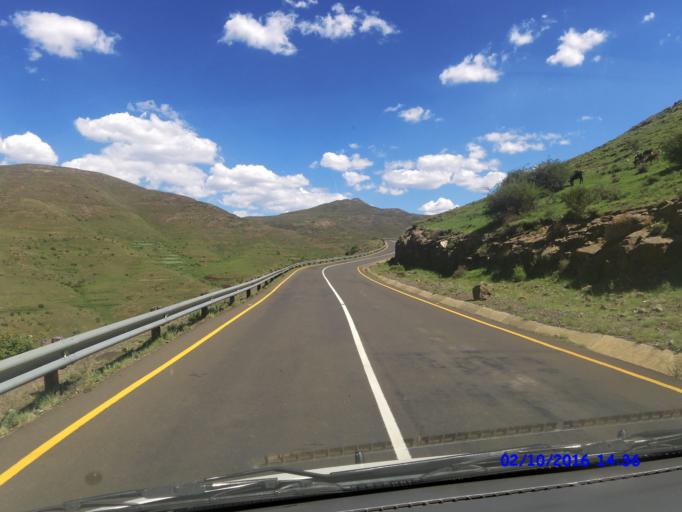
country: LS
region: Maseru
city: Nako
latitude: -29.4961
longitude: 28.0623
